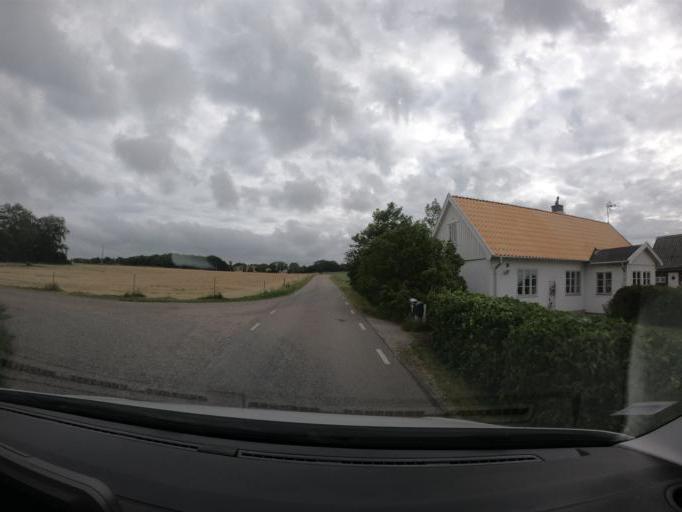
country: SE
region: Skane
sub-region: Bastads Kommun
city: Forslov
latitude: 56.3338
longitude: 12.8104
